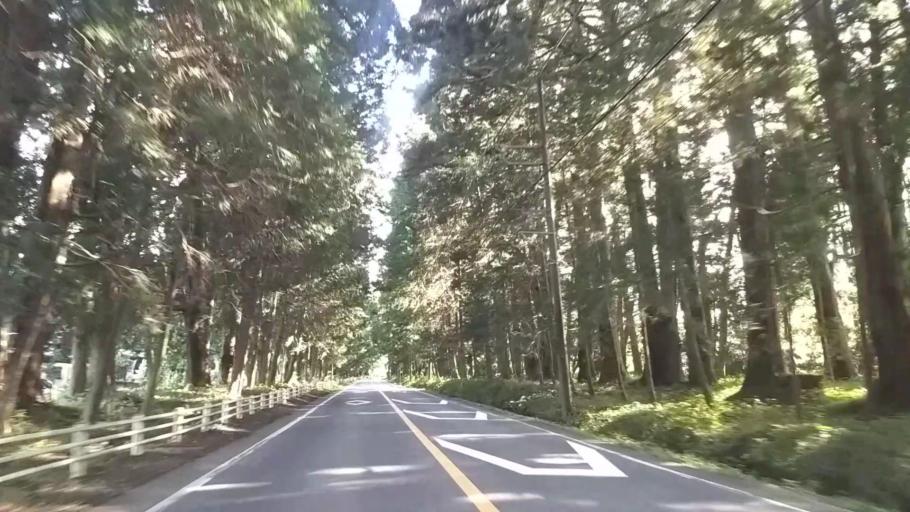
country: JP
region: Tochigi
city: Imaichi
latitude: 36.7528
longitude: 139.7090
